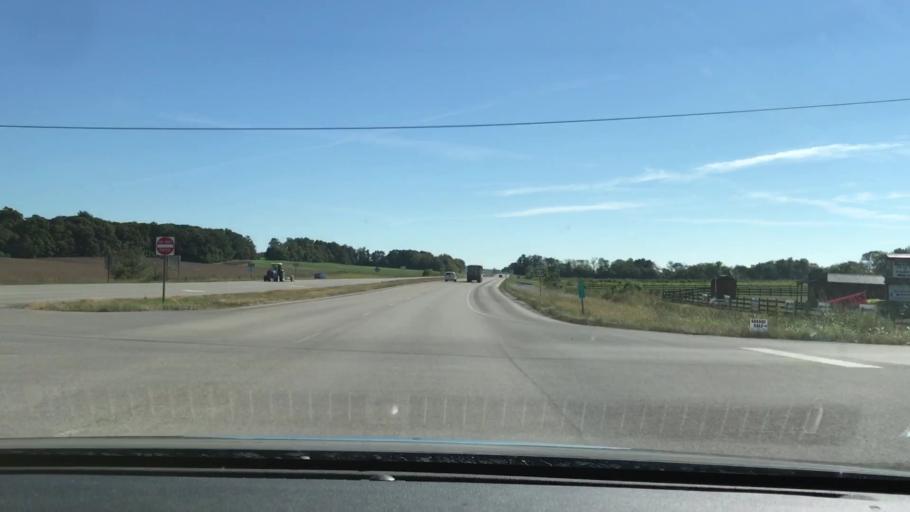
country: US
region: Kentucky
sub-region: Todd County
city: Elkton
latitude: 36.8470
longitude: -87.3012
